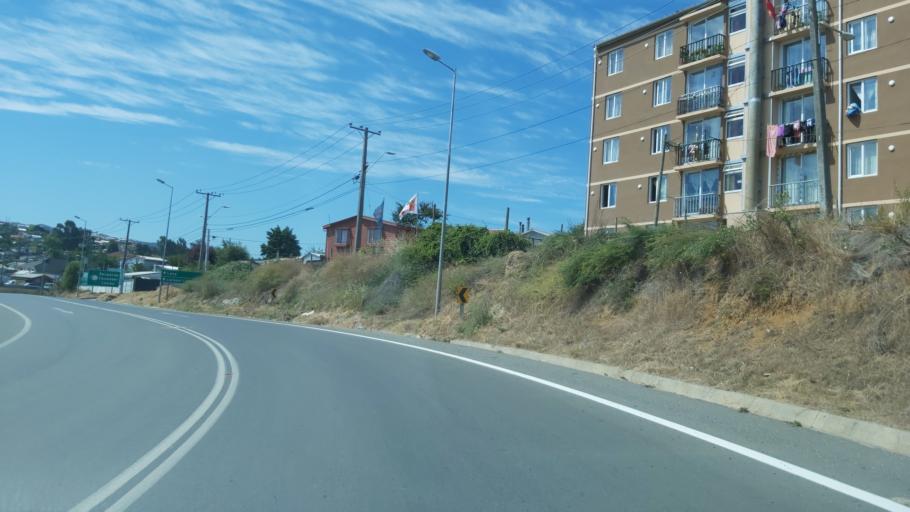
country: CL
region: Biobio
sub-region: Provincia de Concepcion
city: Coronel
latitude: -37.0248
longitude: -73.1366
